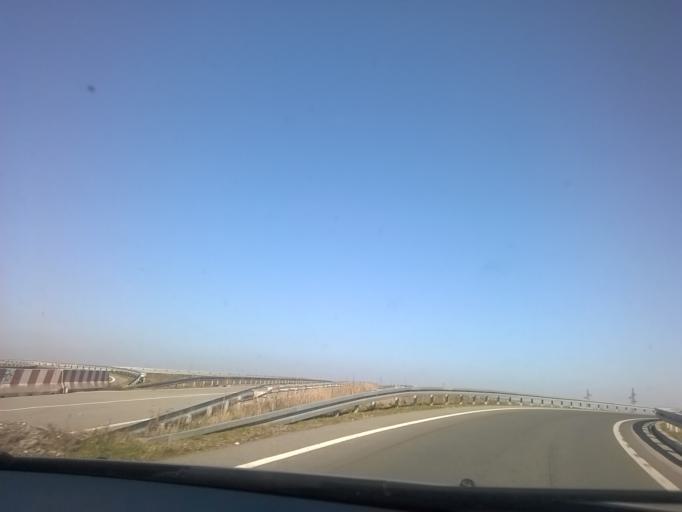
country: RS
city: Pavlis
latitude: 45.1096
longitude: 21.2614
